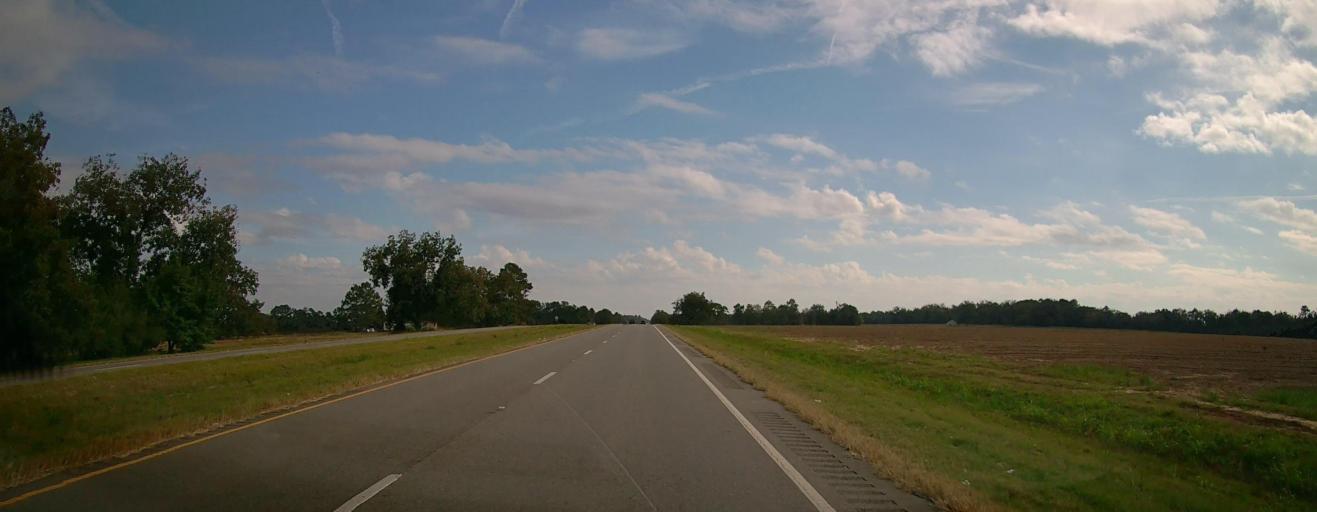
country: US
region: Georgia
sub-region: Thomas County
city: Meigs
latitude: 31.0315
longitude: -84.0630
